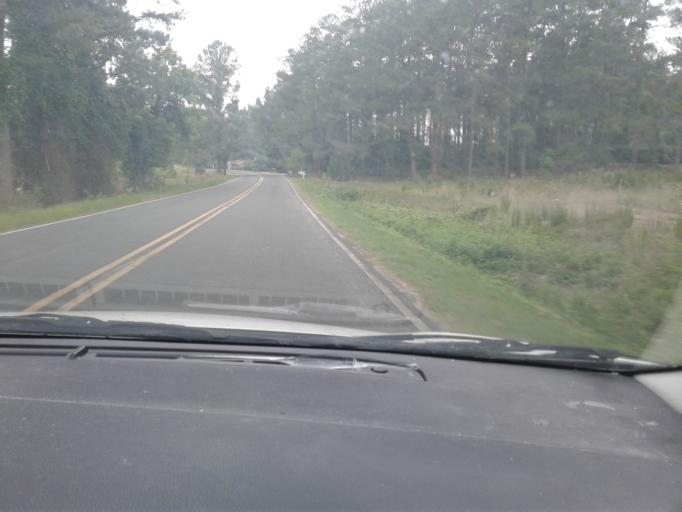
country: US
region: North Carolina
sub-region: Harnett County
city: Coats
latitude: 35.3765
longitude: -78.6511
